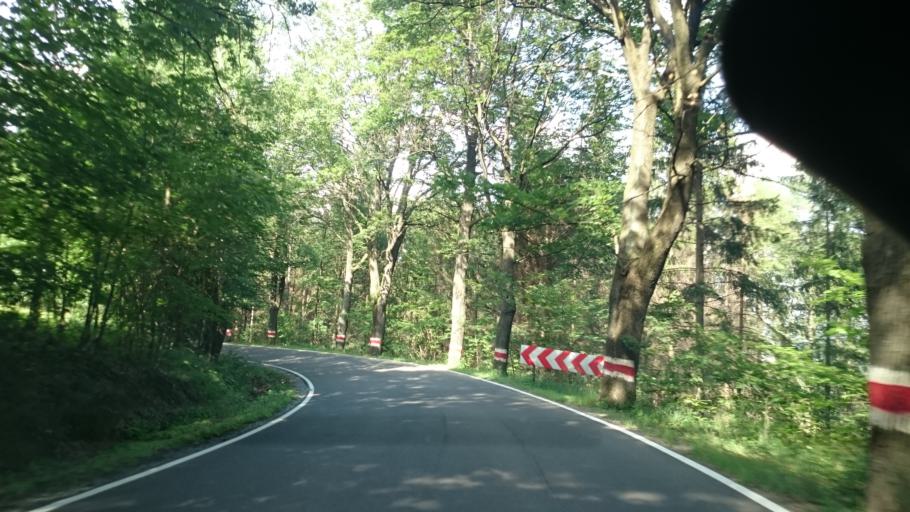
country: PL
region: Lower Silesian Voivodeship
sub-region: Powiat zabkowicki
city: Zloty Stok
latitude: 50.4427
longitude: 16.8572
